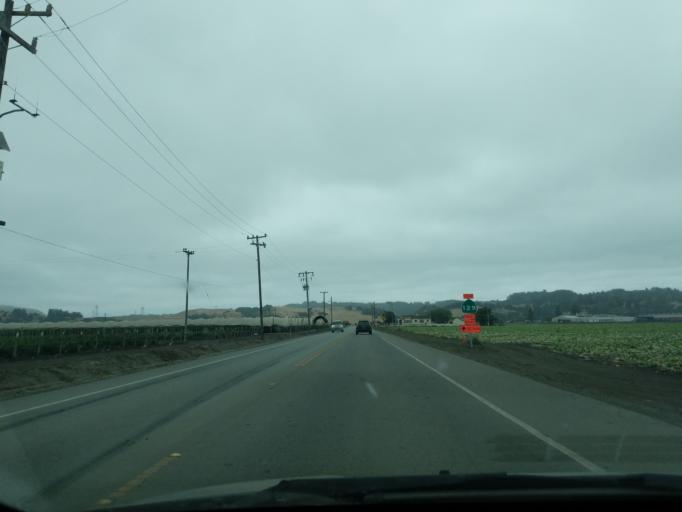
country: US
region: California
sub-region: San Benito County
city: Aromas
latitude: 36.8972
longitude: -121.6798
